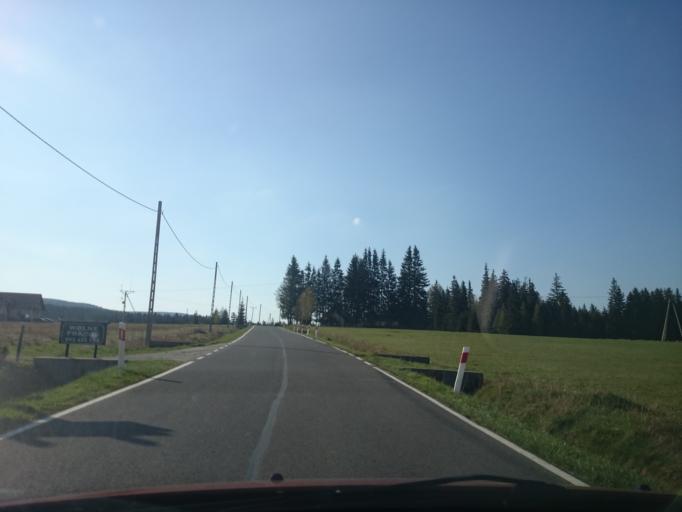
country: PL
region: Lower Silesian Voivodeship
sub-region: Powiat klodzki
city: Szczytna
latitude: 50.3164
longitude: 16.4434
